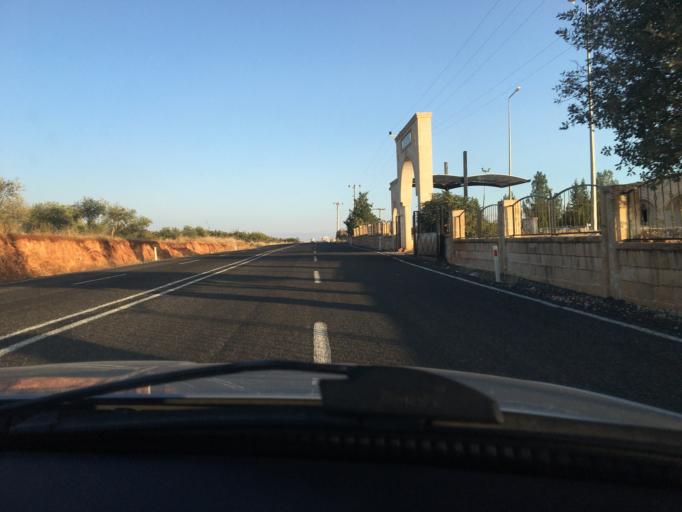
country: TR
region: Sanliurfa
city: Halfeti
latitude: 37.2410
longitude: 37.9106
